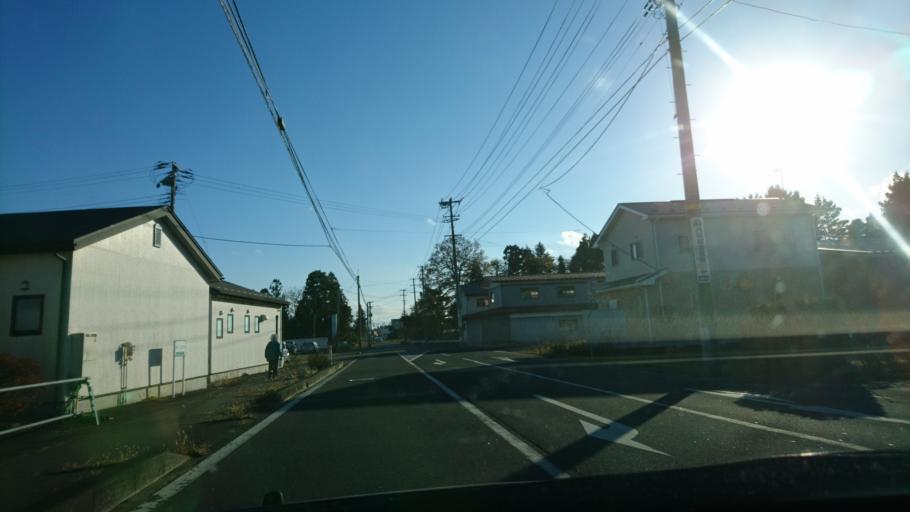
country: JP
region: Iwate
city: Mizusawa
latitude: 39.1189
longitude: 141.1557
